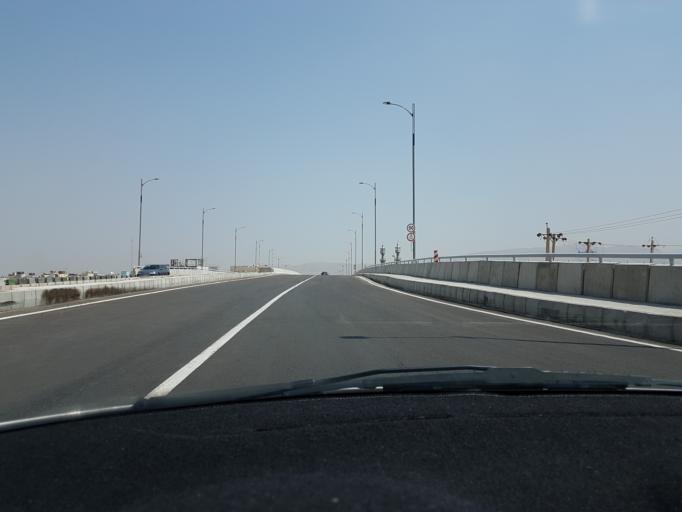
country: IR
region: Fars
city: Shiraz
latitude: 29.6304
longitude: 52.4557
